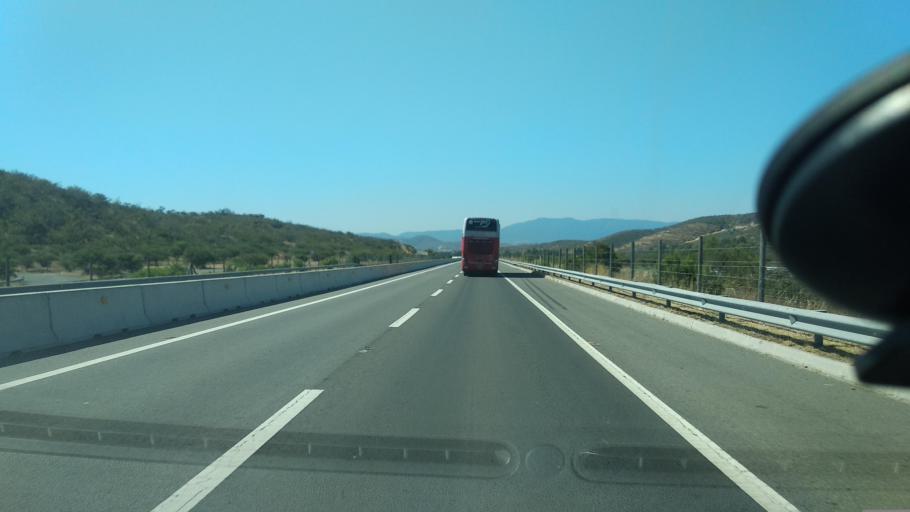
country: CL
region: Valparaiso
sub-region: Provincia de Marga Marga
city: Limache
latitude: -33.0220
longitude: -71.3191
